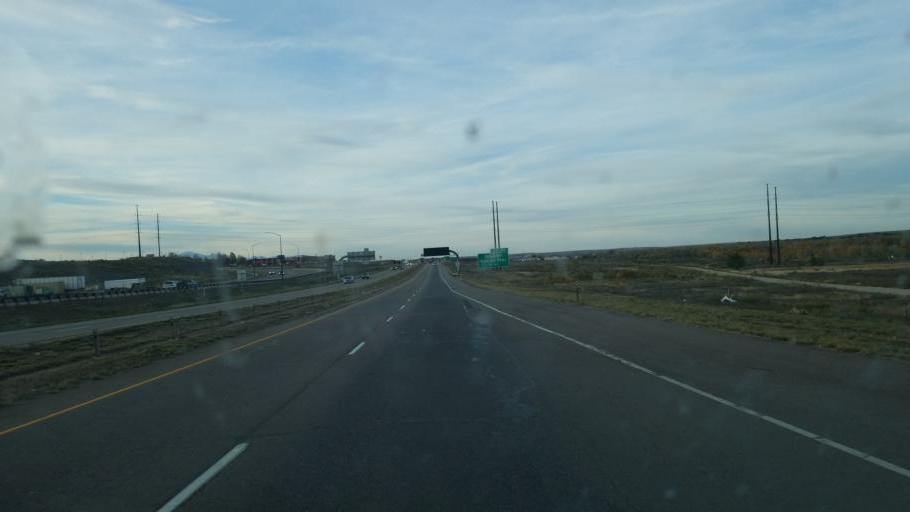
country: US
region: Colorado
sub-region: Pueblo County
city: Pueblo
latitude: 38.3269
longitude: -104.6161
